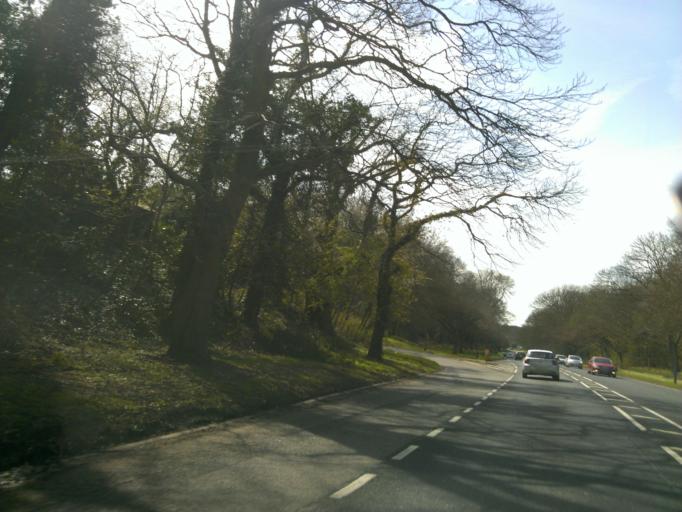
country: GB
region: England
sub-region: Essex
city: West Bergholt
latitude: 51.8938
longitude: 0.8728
